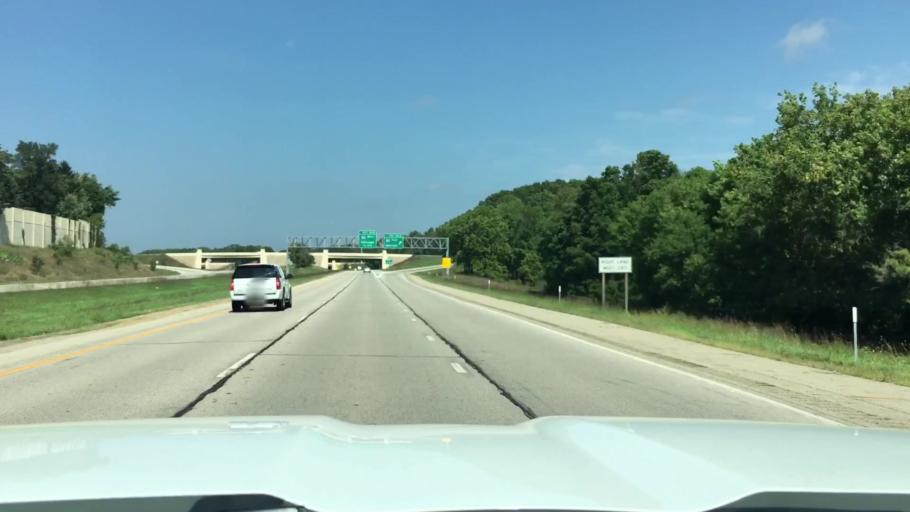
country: US
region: Michigan
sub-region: Kalamazoo County
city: Portage
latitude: 42.2315
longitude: -85.6383
